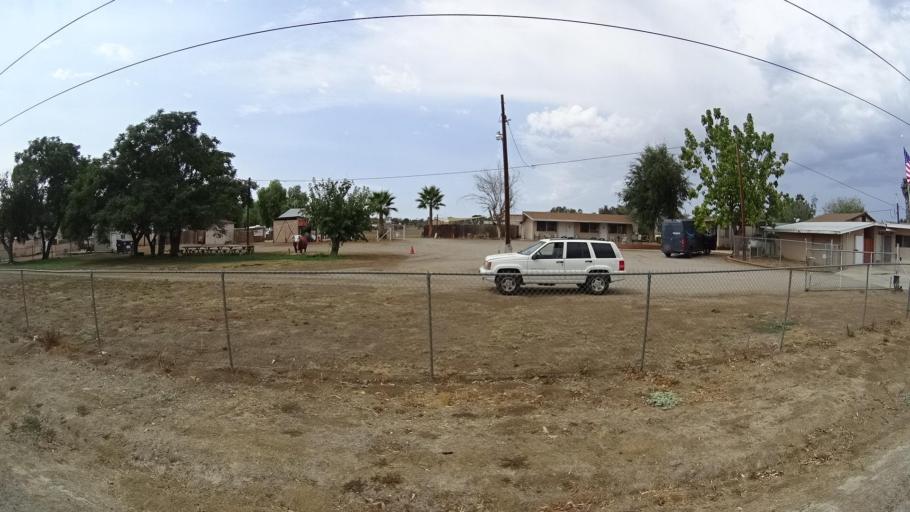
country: US
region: California
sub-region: San Diego County
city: Ramona
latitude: 33.0610
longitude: -116.8608
